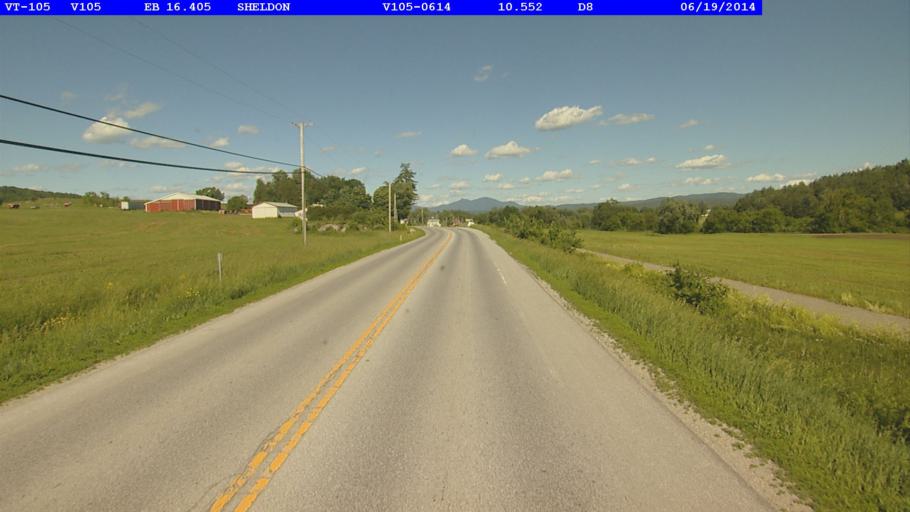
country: US
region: Vermont
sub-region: Franklin County
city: Enosburg Falls
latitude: 44.9072
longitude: -72.8289
